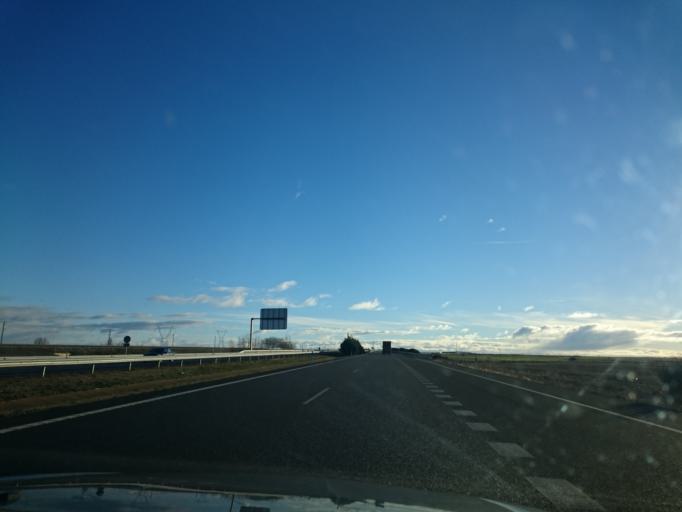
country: ES
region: Castille and Leon
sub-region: Provincia de Leon
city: Vallecillo
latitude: 42.4142
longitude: -5.2111
